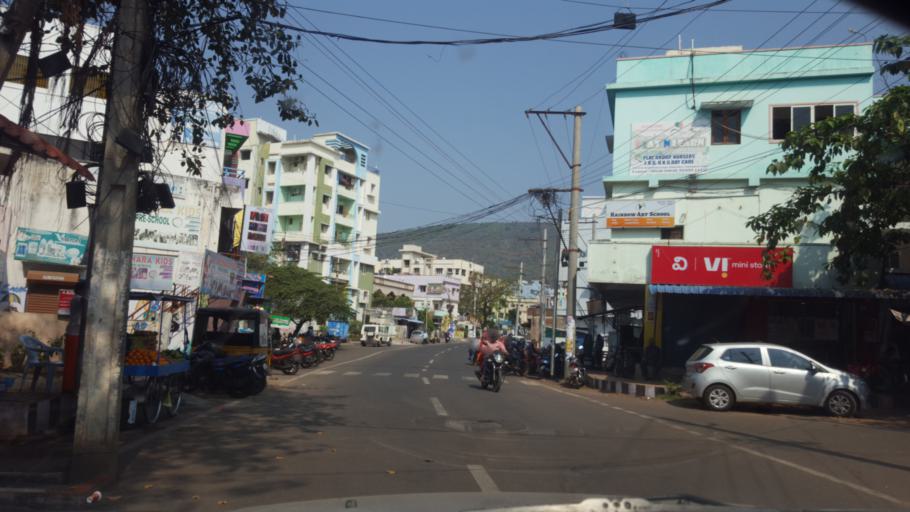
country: IN
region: Andhra Pradesh
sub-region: Vishakhapatnam
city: Vepagunta
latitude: 17.7449
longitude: 83.2587
